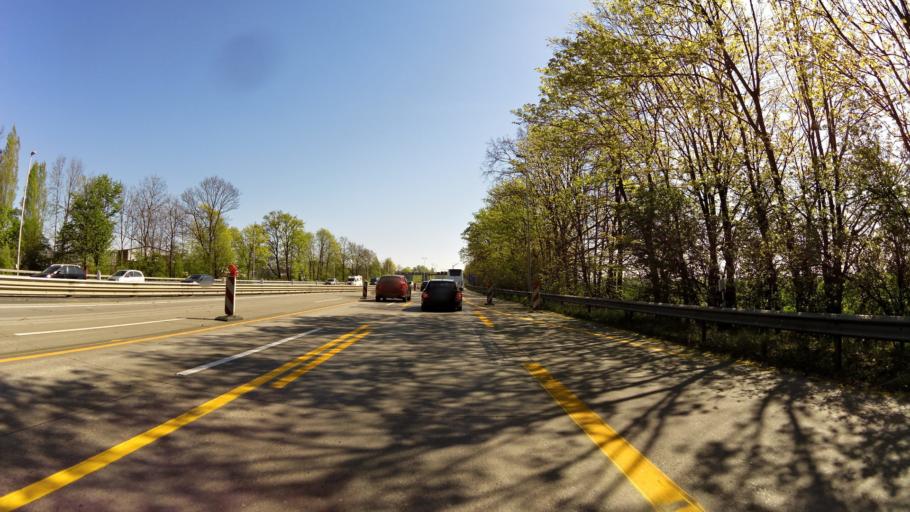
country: DE
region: Bremen
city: Bremen
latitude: 53.0235
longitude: 8.8080
